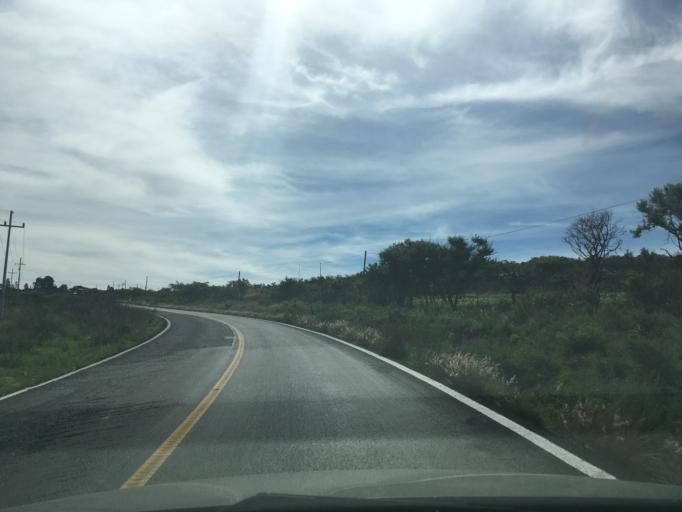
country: MX
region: Guanajuato
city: Coroneo
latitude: 20.1883
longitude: -100.4198
